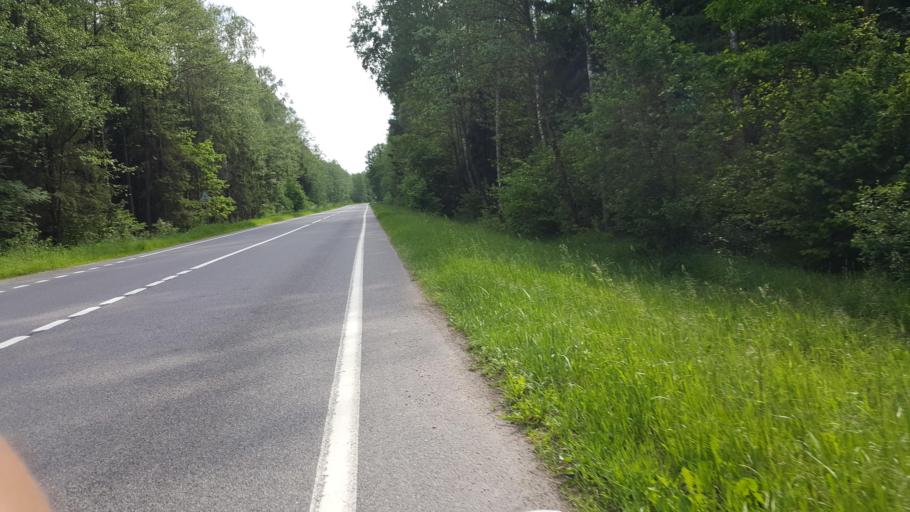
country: BY
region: Brest
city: Pruzhany
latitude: 52.4860
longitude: 24.1694
